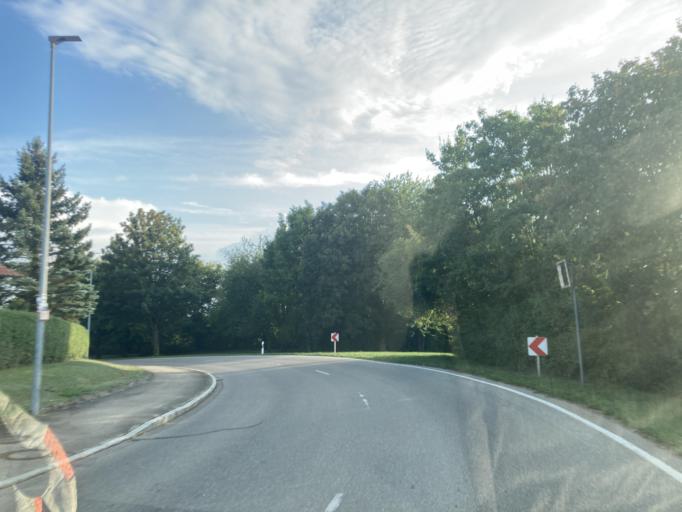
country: DE
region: Bavaria
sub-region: Swabia
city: Medlingen
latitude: 48.5730
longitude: 10.3128
